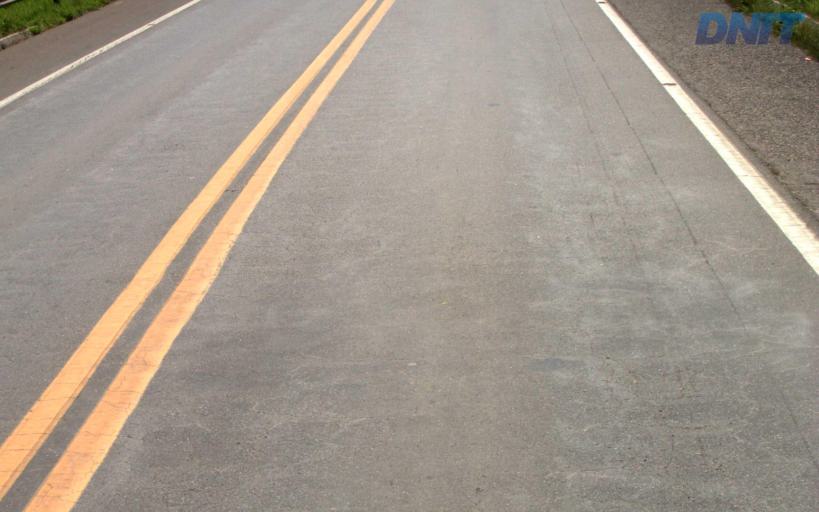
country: BR
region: Minas Gerais
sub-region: Governador Valadares
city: Governador Valadares
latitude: -19.0665
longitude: -42.1710
